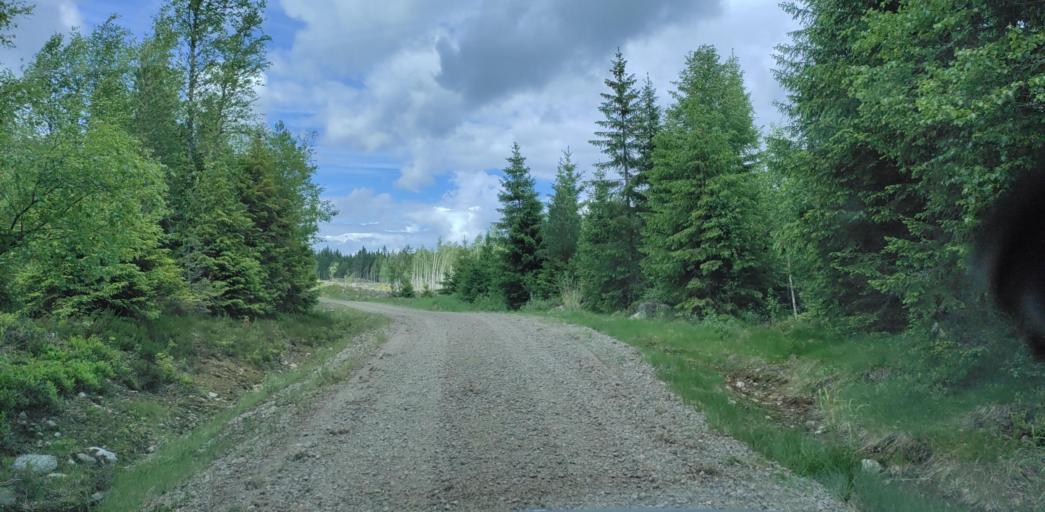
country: SE
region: Vaermland
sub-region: Munkfors Kommun
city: Munkfors
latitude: 59.9435
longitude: 13.4230
